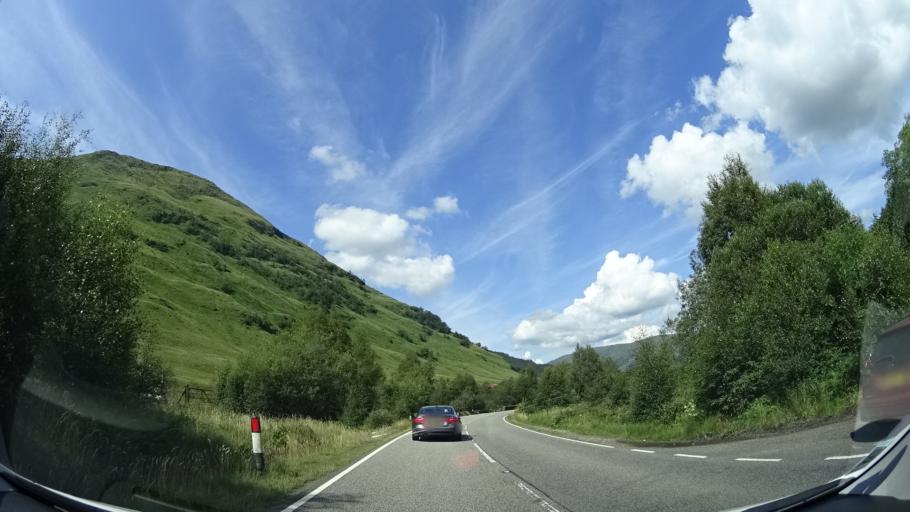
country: GB
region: Scotland
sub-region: Highland
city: Fort William
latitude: 56.6611
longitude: -5.0689
